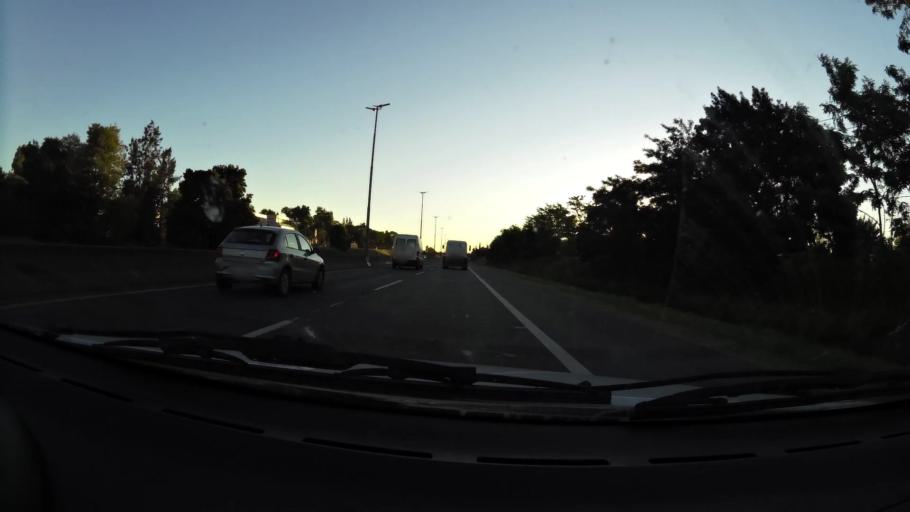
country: AR
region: Buenos Aires
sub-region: Partido de Quilmes
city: Quilmes
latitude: -34.8113
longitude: -58.1769
